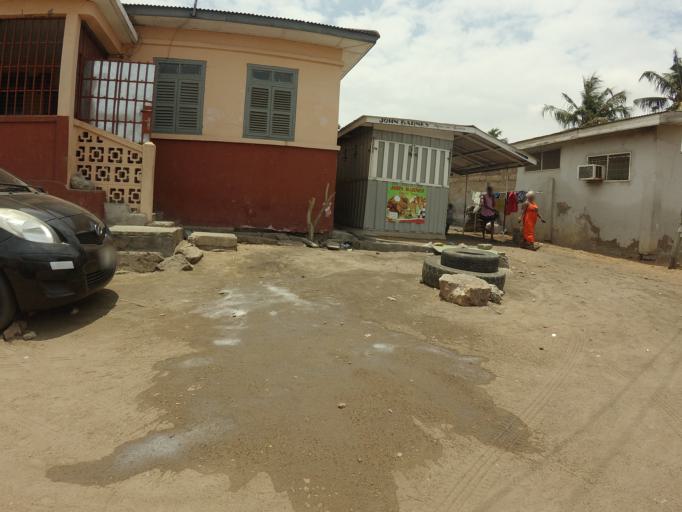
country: GH
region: Greater Accra
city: Nungua
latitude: 5.6001
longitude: -0.0821
